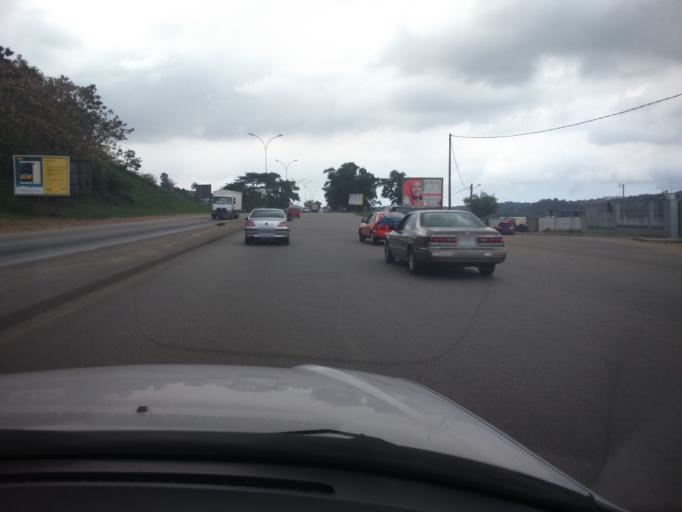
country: CI
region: Lagunes
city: Abidjan
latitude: 5.3567
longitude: -4.0403
